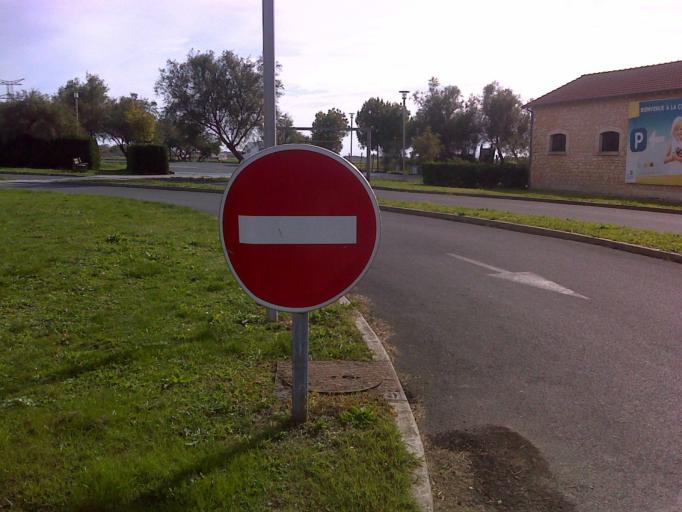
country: FR
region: Poitou-Charentes
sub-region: Departement de la Charente-Maritime
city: Marennes
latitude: 45.8129
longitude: -1.1132
